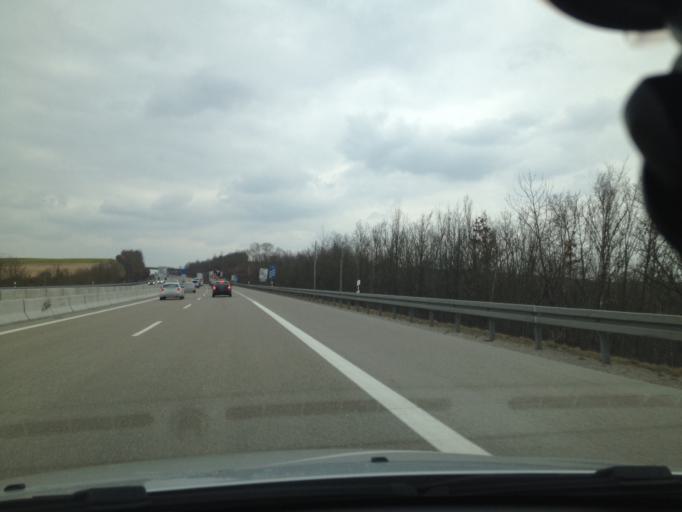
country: DE
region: Bavaria
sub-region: Regierungsbezirk Unterfranken
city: Obernbreit
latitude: 49.6446
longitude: 10.1630
